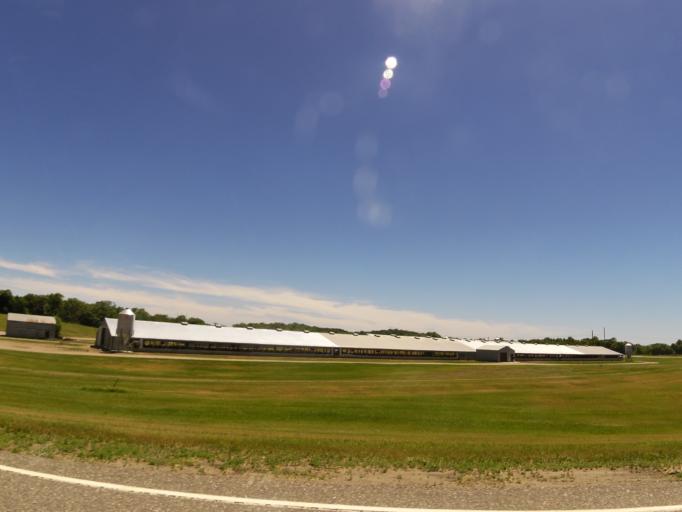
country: US
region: Minnesota
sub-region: Becker County
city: Frazee
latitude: 46.7219
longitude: -95.7137
